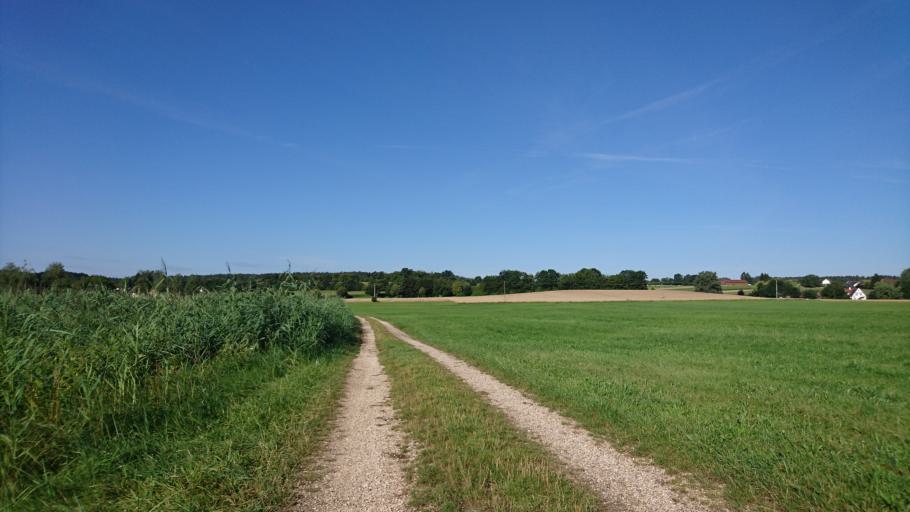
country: DE
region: Bavaria
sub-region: Swabia
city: Altenmunster
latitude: 48.4430
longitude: 10.5957
